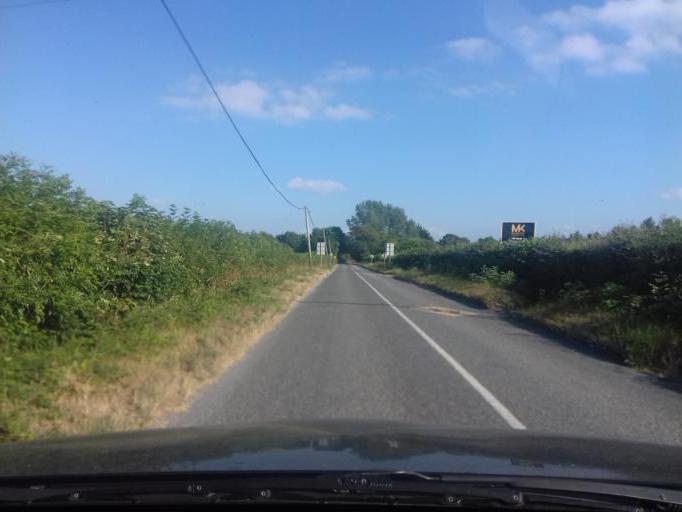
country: IE
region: Leinster
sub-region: An Mhi
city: Ashbourne
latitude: 53.4498
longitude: -6.3942
